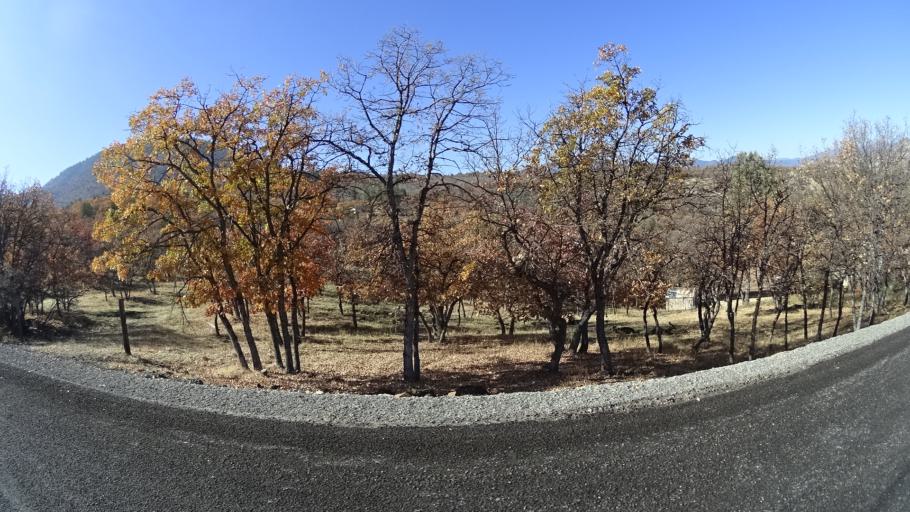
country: US
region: California
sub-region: Siskiyou County
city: Montague
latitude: 41.8815
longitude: -122.4899
